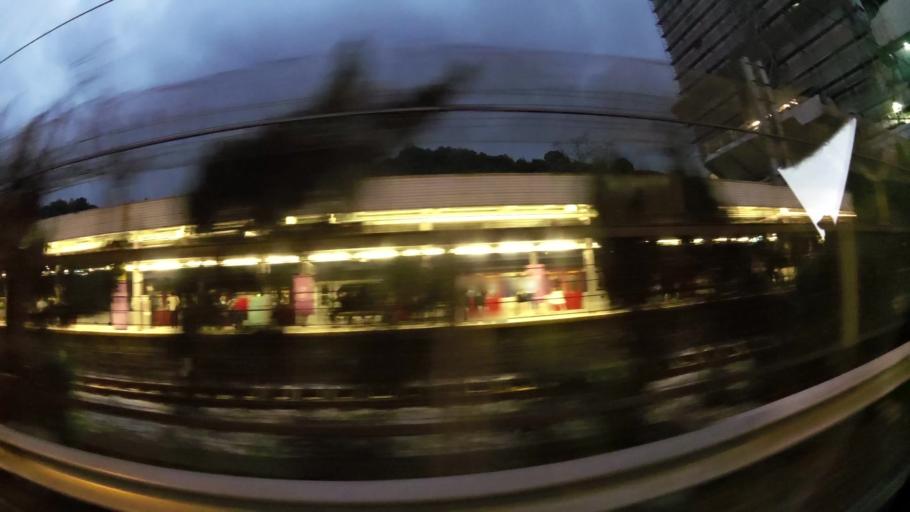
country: HK
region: Sha Tin
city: Sha Tin
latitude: 22.3820
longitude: 114.1872
